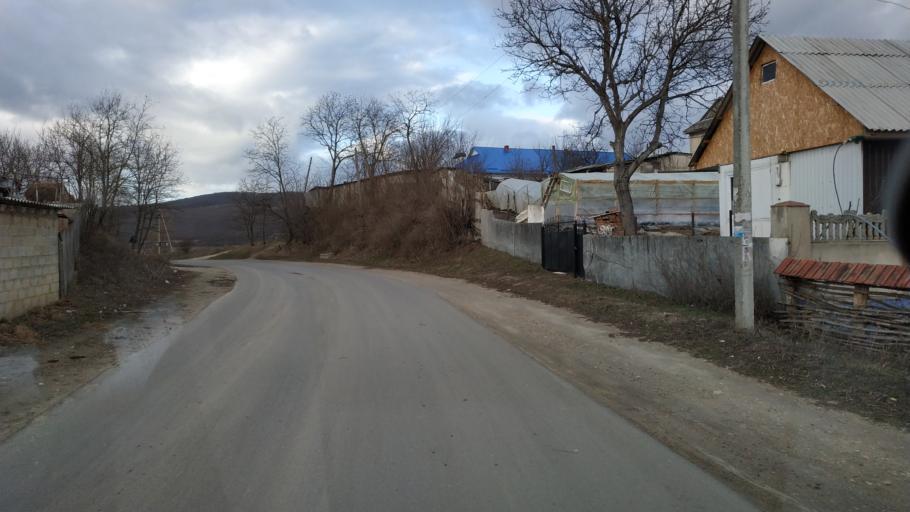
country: MD
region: Calarasi
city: Calarasi
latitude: 47.3069
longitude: 28.3608
